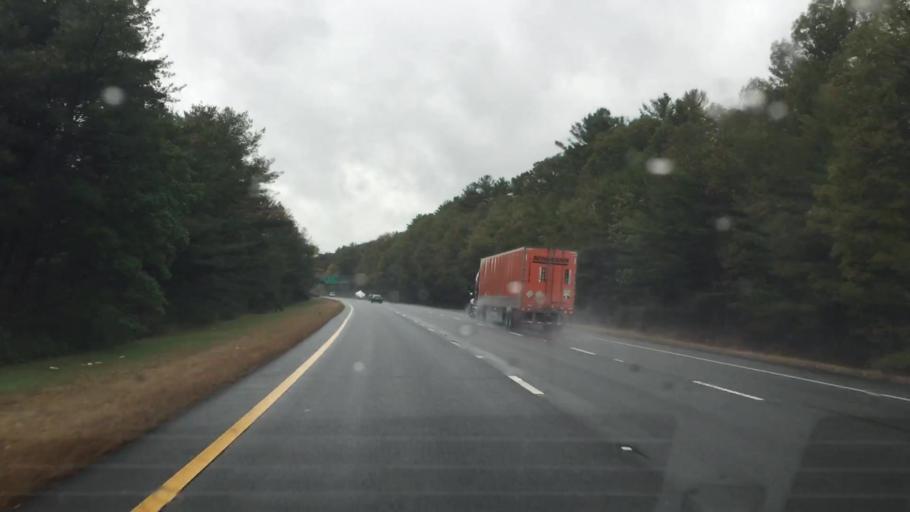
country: US
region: Massachusetts
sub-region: Essex County
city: Merrimac
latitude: 42.8343
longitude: -70.9746
